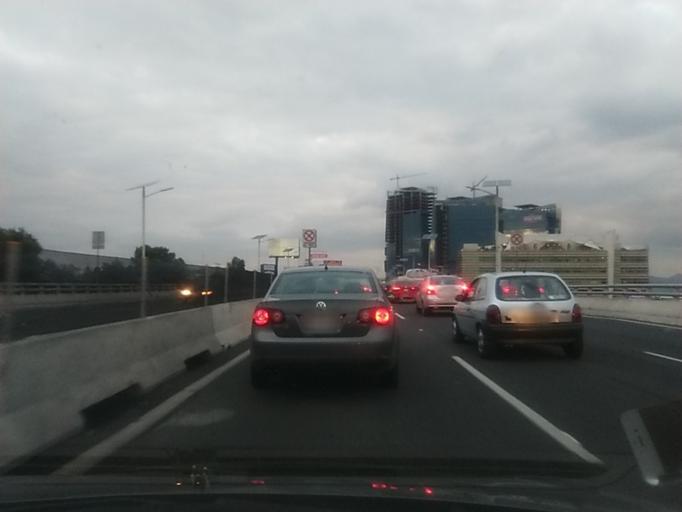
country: MX
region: Mexico City
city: Miguel Hidalgo
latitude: 19.4488
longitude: -99.2202
